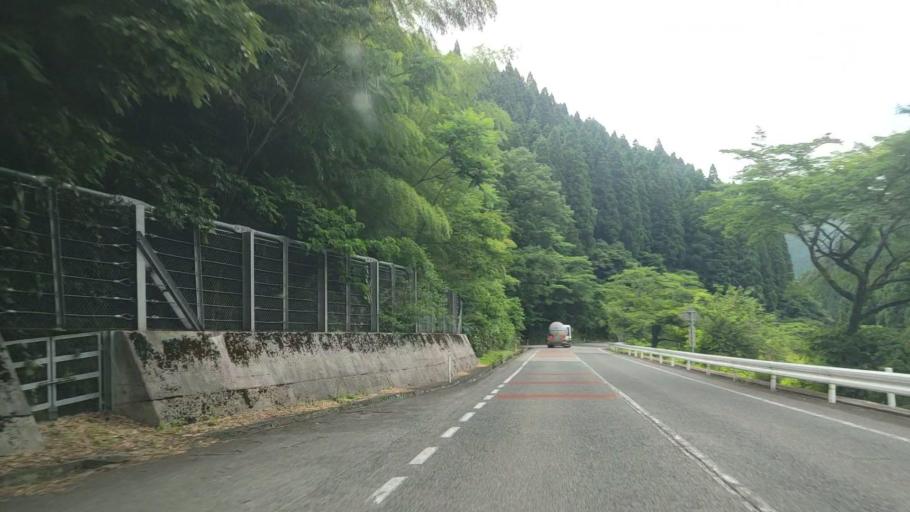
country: JP
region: Tottori
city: Yonago
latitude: 35.2548
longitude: 133.4377
